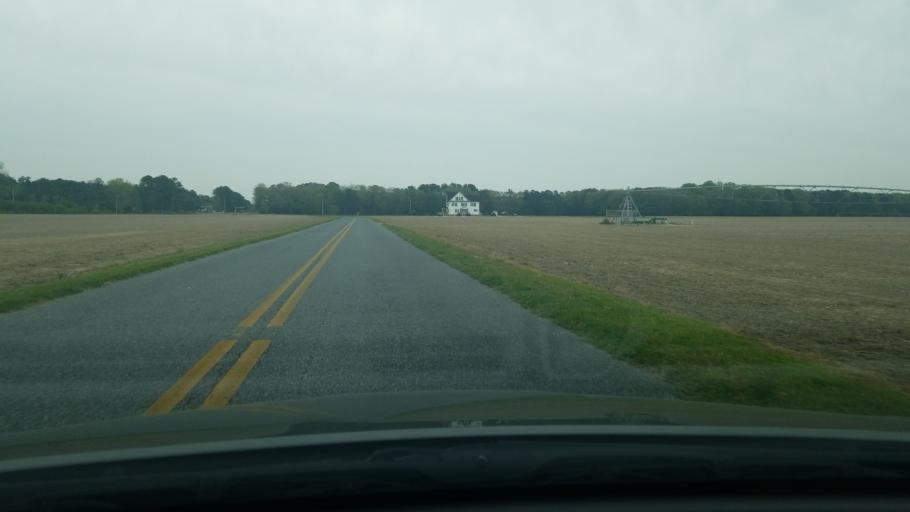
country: US
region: Maryland
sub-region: Worcester County
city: Snow Hill
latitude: 38.2385
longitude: -75.3061
